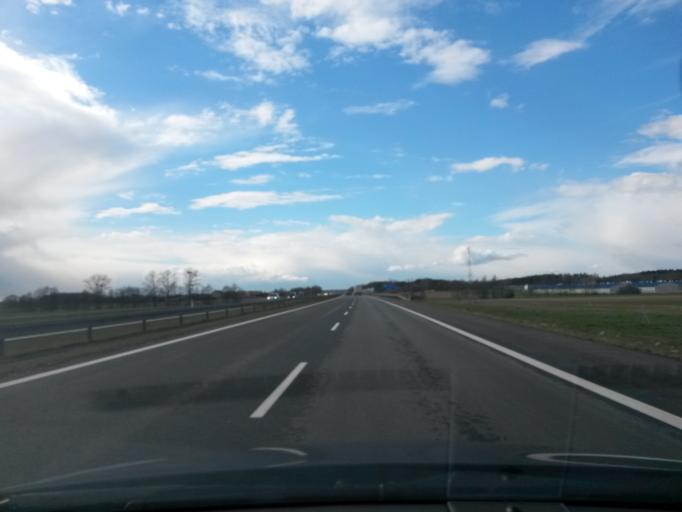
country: PL
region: Greater Poland Voivodeship
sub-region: Powiat slupecki
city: Slupca
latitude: 52.2409
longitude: 17.8781
